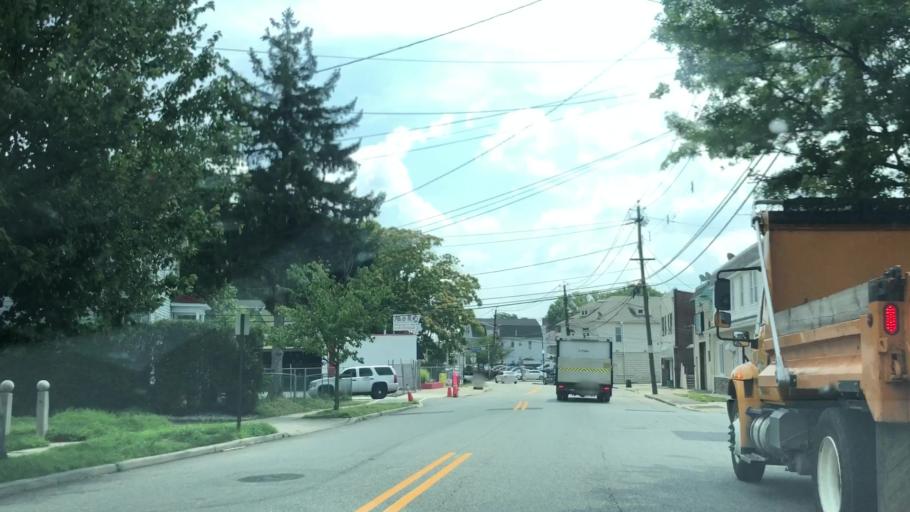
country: US
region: New Jersey
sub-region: Essex County
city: Orange
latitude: 40.7844
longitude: -74.2264
